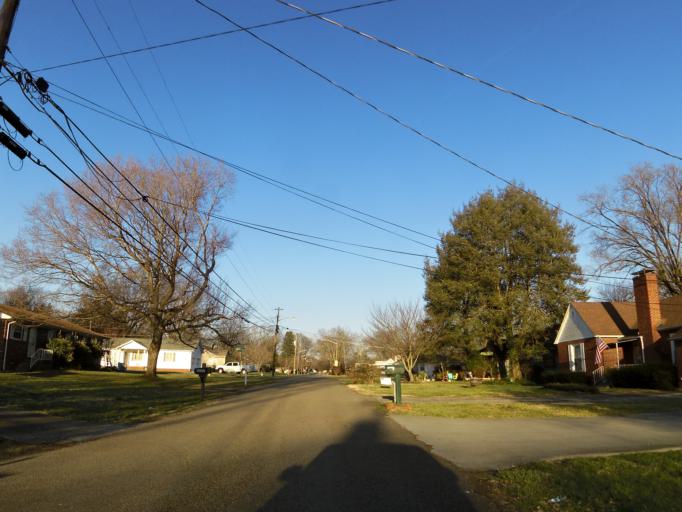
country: US
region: Tennessee
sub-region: Knox County
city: Knoxville
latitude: 36.0137
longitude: -83.9057
